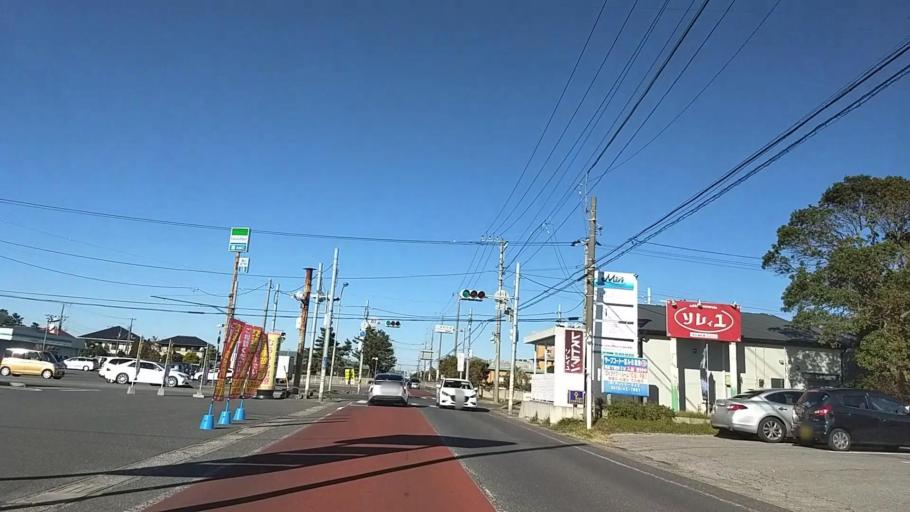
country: JP
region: Chiba
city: Mobara
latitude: 35.3729
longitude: 140.3876
